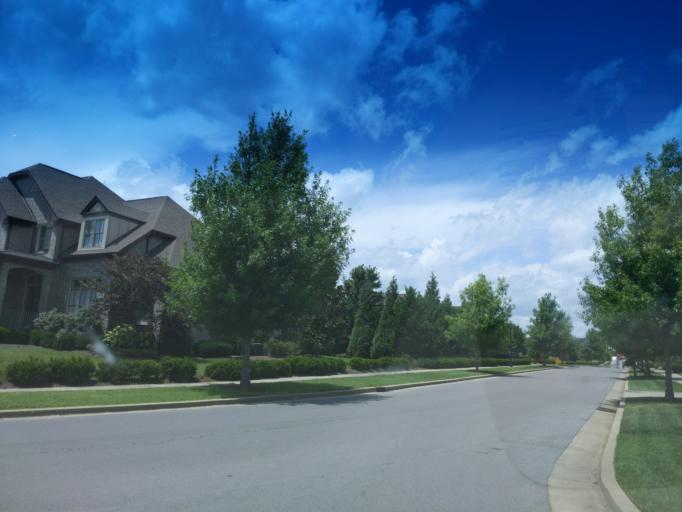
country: US
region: Tennessee
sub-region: Williamson County
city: Brentwood Estates
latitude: 36.0194
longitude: -86.7672
